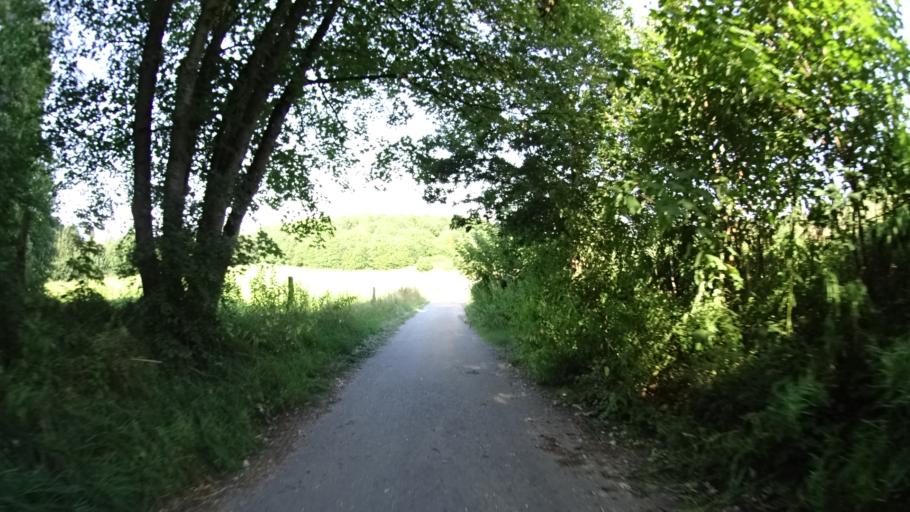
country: DK
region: Central Jutland
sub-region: Arhus Kommune
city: Stavtrup
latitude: 56.1609
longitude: 10.1121
